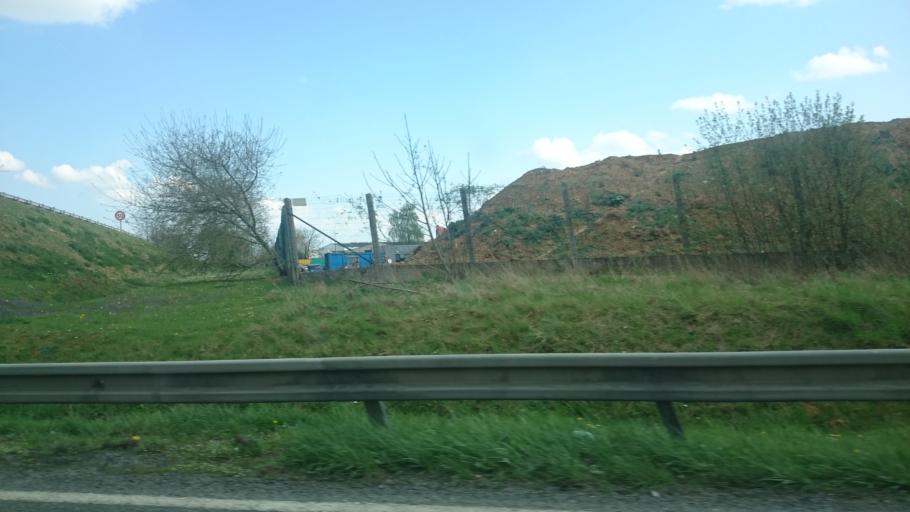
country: FR
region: Picardie
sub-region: Departement de l'Aisne
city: Gauchy
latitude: 49.8187
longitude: 3.2936
